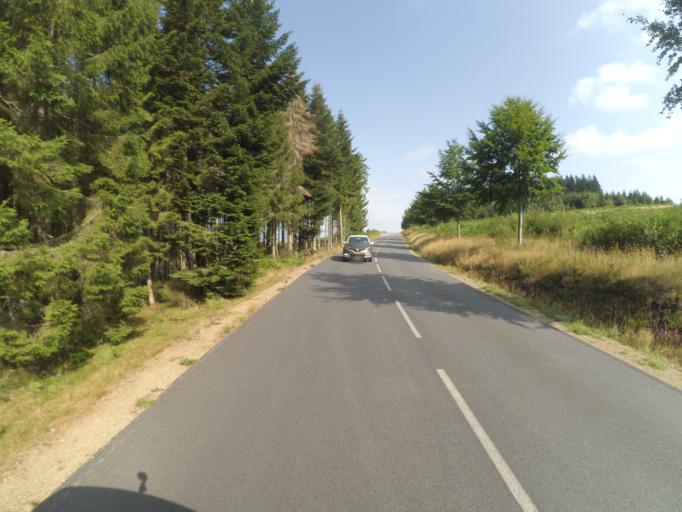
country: FR
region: Limousin
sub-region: Departement de la Correze
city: Meymac
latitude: 45.6093
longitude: 2.1096
